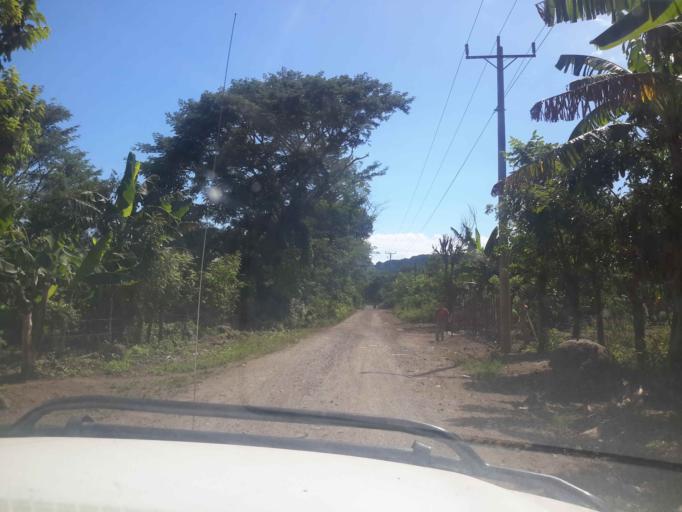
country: NI
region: Rivas
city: Altagracia
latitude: 11.4662
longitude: -85.4647
